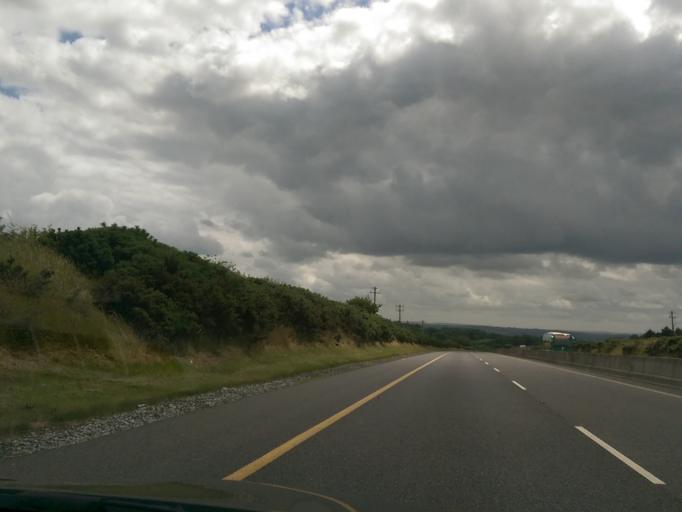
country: IE
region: Munster
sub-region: County Cork
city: Mitchelstown
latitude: 52.2114
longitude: -8.2765
